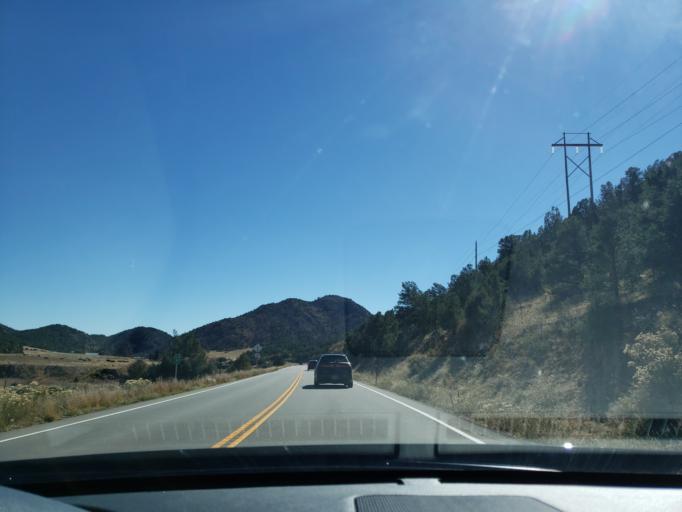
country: US
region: Colorado
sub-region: Fremont County
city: Canon City
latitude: 38.5902
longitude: -105.4238
